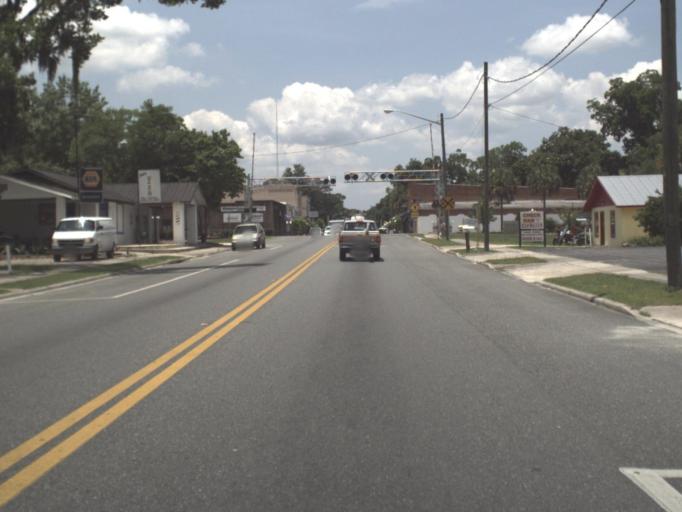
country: US
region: Florida
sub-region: Alachua County
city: Newberry
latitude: 29.6464
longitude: -82.6095
